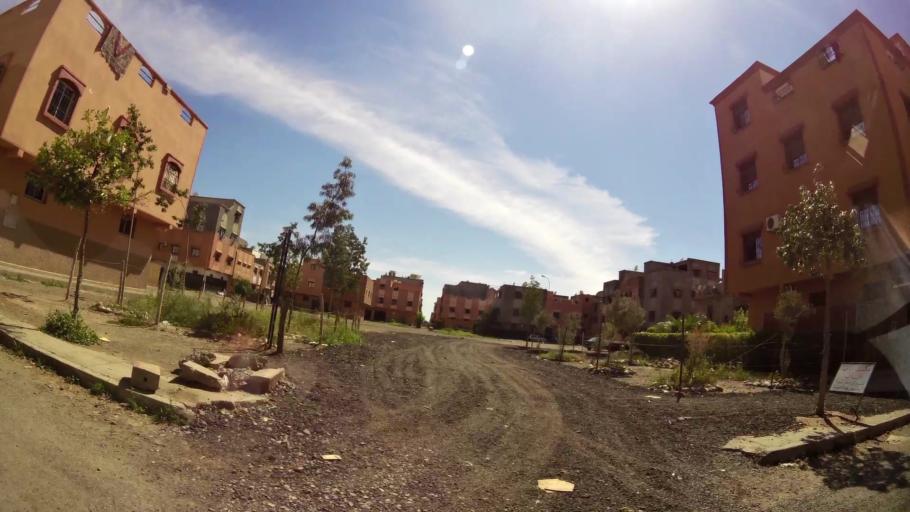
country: MA
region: Marrakech-Tensift-Al Haouz
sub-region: Marrakech
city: Marrakesh
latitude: 31.6411
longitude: -8.1099
